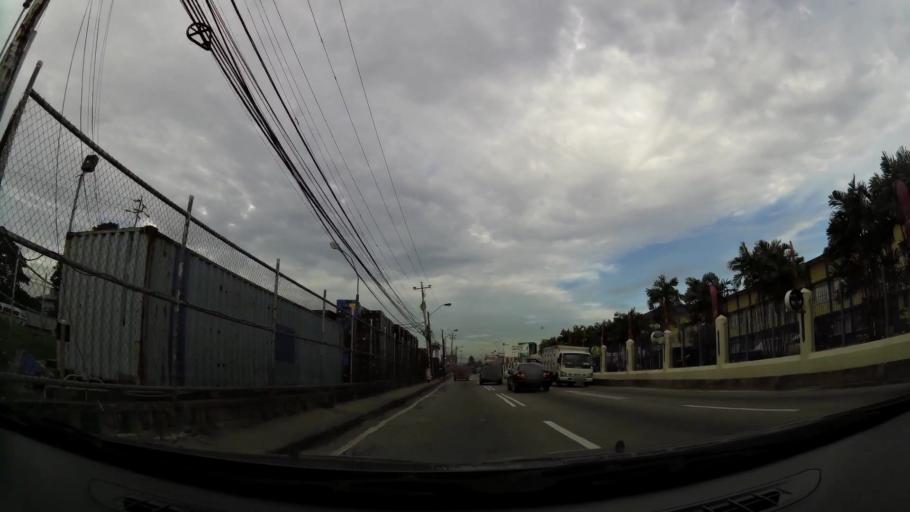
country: TT
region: Tunapuna/Piarco
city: Tunapuna
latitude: 10.6502
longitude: -61.4267
